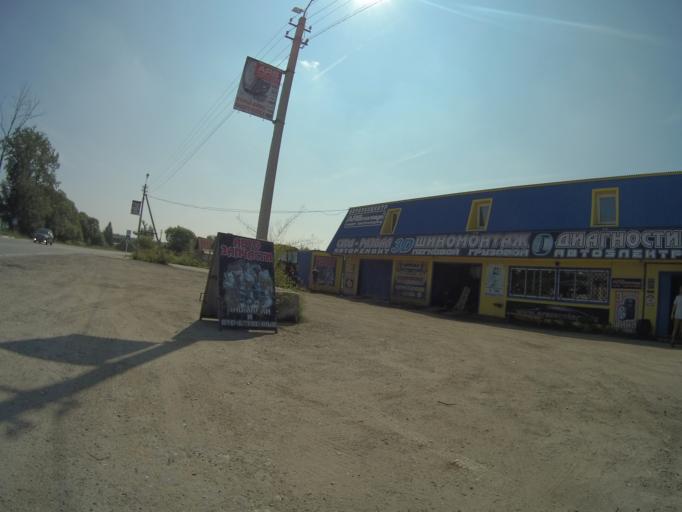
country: RU
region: Vladimir
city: Anopino
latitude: 55.7424
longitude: 40.7004
